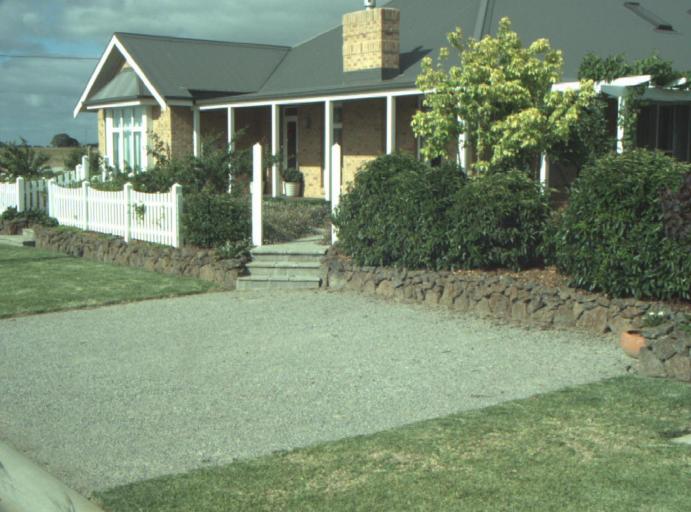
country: AU
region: Victoria
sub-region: Greater Geelong
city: Wandana Heights
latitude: -38.2140
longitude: 144.2945
